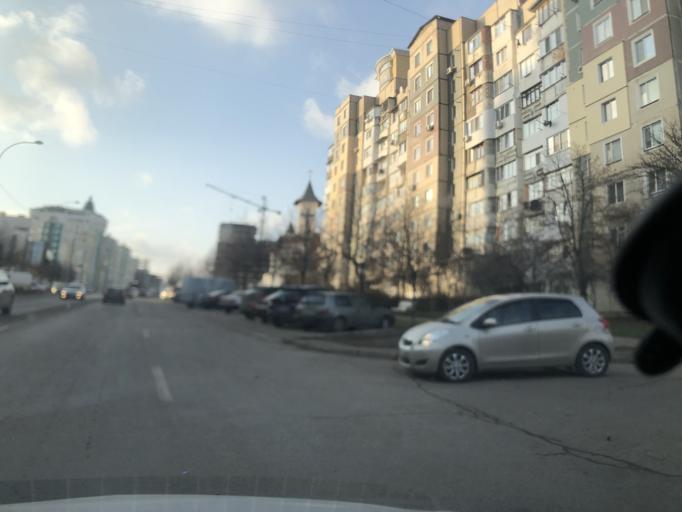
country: MD
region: Chisinau
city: Stauceni
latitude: 47.0567
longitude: 28.8942
